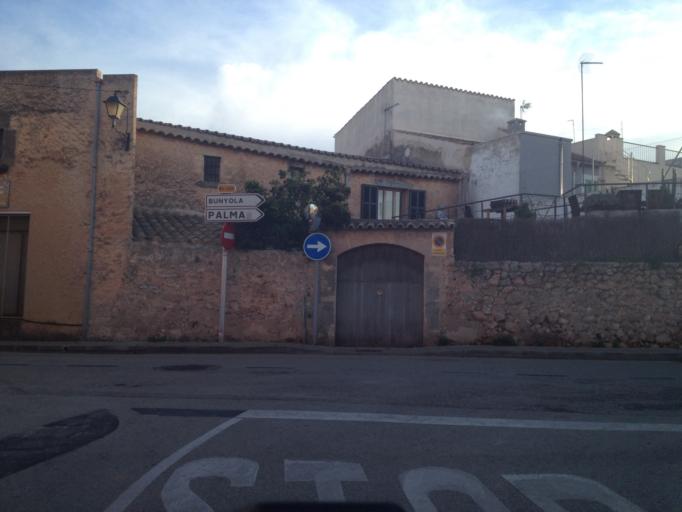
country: ES
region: Balearic Islands
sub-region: Illes Balears
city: Santa Maria del Cami
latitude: 39.6511
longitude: 2.7715
